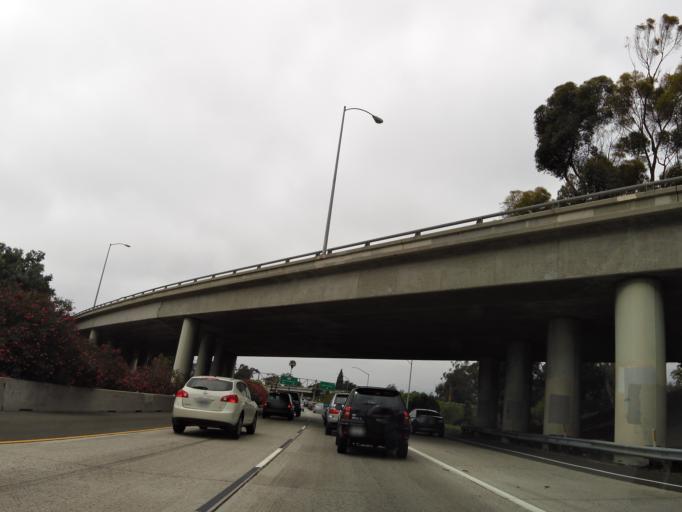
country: US
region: California
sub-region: Ventura County
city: Ventura
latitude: 34.2649
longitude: -119.2368
